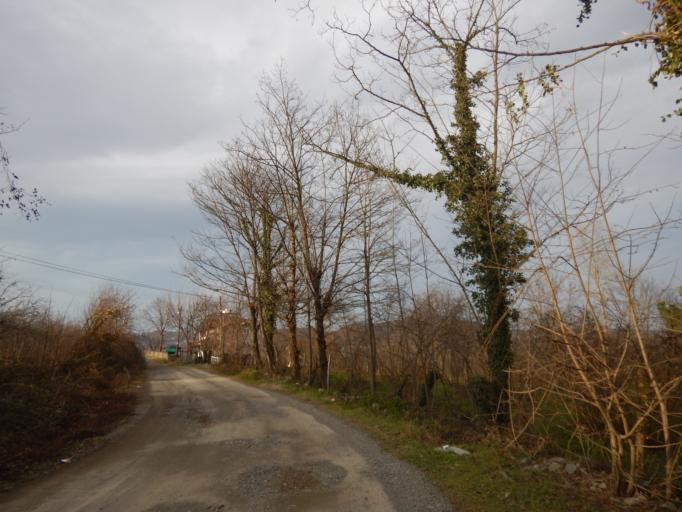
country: TR
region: Ordu
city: Uzunisa
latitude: 40.9047
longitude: 37.8079
